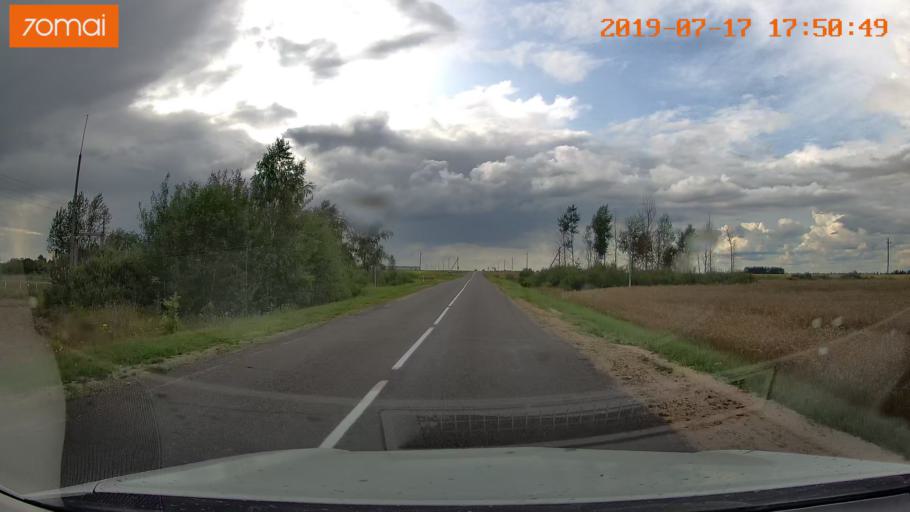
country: BY
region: Mogilev
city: Hlusha
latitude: 53.1454
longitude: 28.7967
